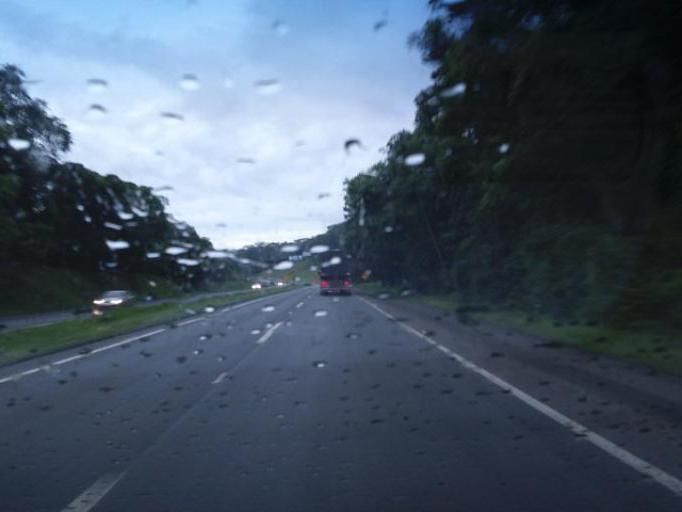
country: BR
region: Santa Catarina
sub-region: Joinville
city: Joinville
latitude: -26.0020
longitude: -48.8744
